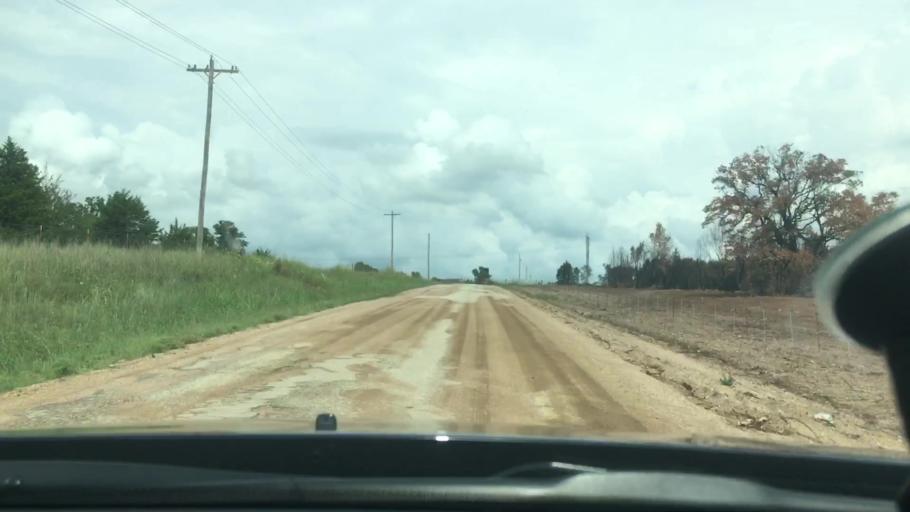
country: US
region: Oklahoma
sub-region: Carter County
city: Dickson
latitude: 34.2434
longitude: -96.9173
